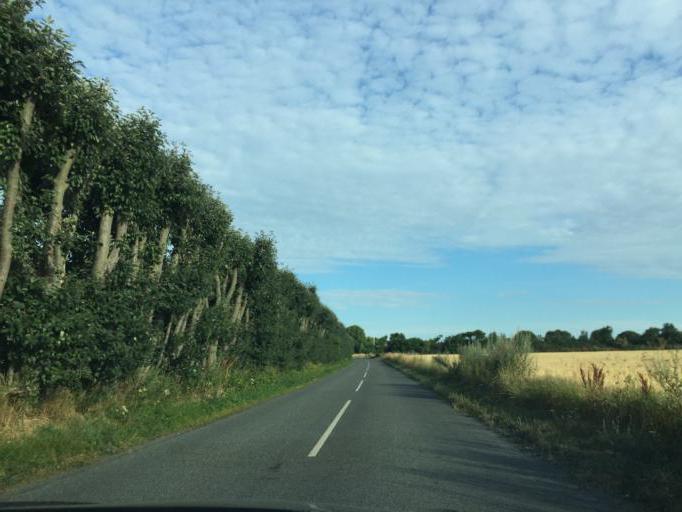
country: DK
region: South Denmark
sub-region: Assens Kommune
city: Harby
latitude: 55.1564
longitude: 10.0035
